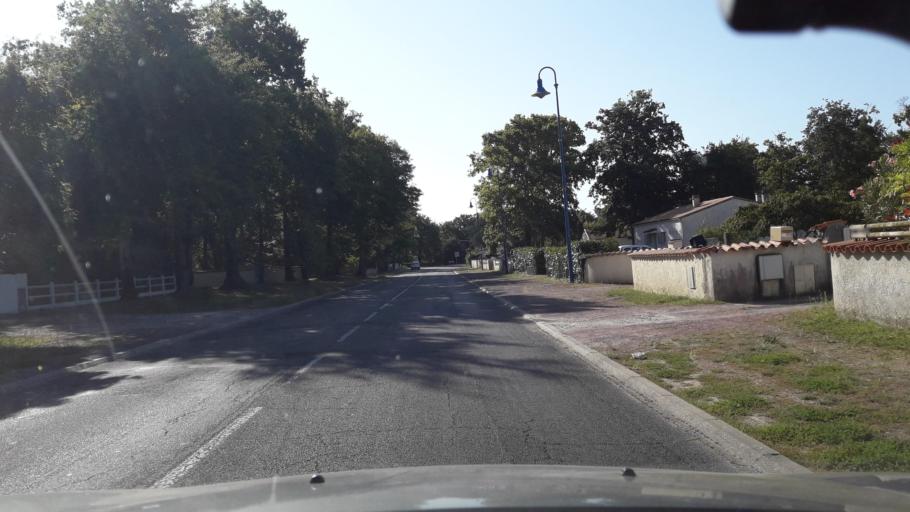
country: FR
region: Poitou-Charentes
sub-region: Departement de la Charente-Maritime
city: Etaules
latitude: 45.7287
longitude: -1.0921
